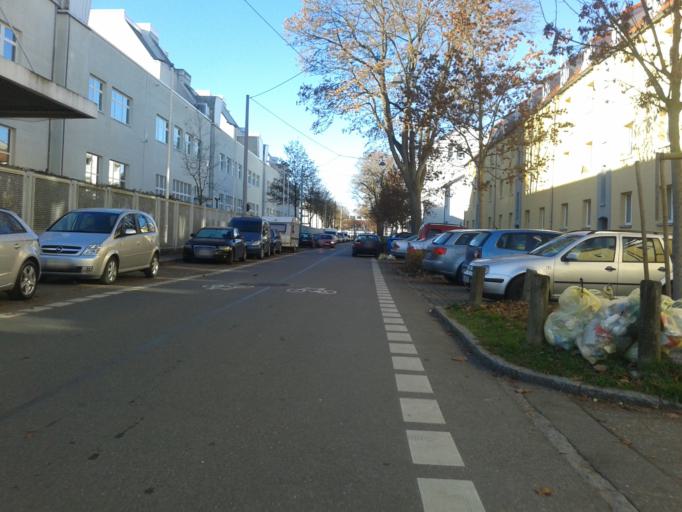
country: DE
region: Baden-Wuerttemberg
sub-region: Tuebingen Region
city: Ulm
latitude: 48.3929
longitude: 9.9708
